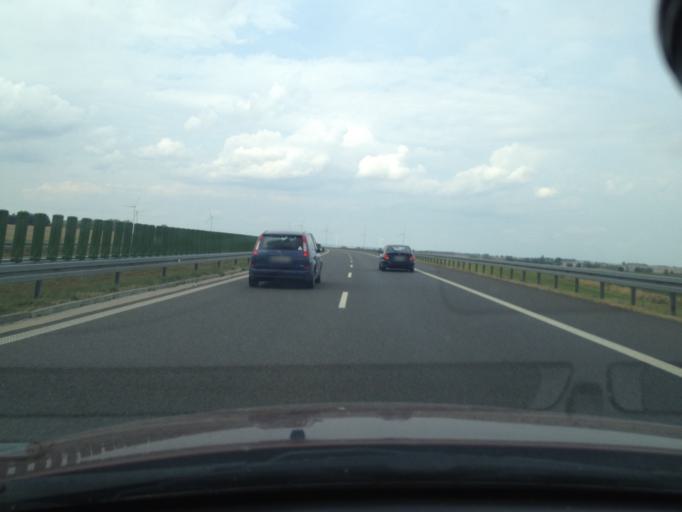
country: PL
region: West Pomeranian Voivodeship
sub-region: Powiat pyrzycki
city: Kozielice
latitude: 53.0718
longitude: 14.8606
